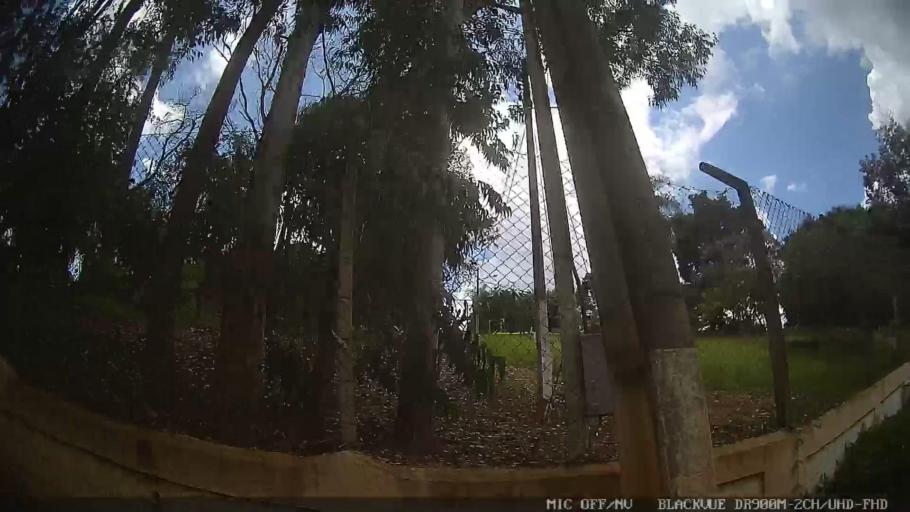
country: BR
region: Sao Paulo
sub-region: Atibaia
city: Atibaia
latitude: -23.1292
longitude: -46.6346
